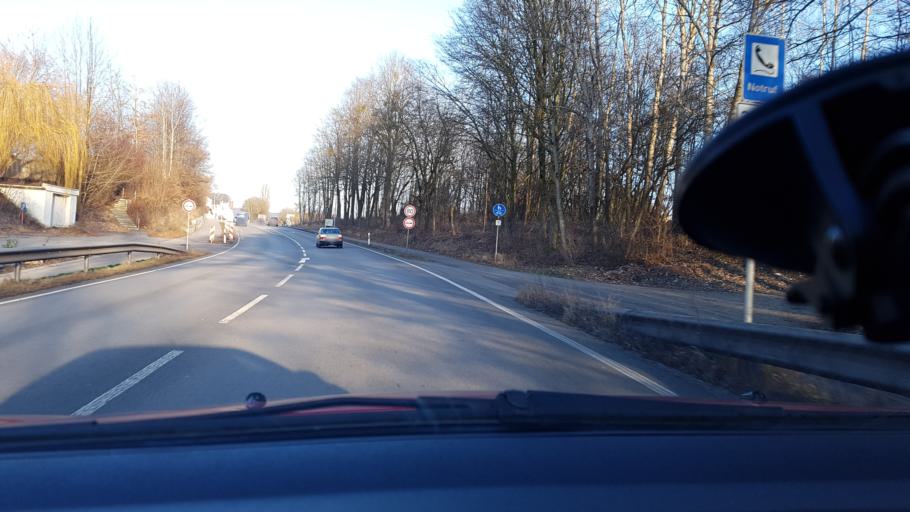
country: DE
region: Bavaria
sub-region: Lower Bavaria
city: Stubenberg
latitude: 48.2841
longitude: 13.0783
